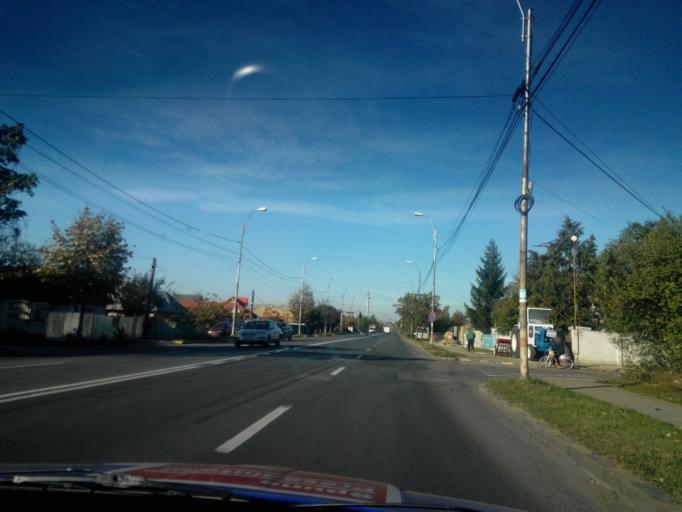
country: RO
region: Bacau
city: Margineni-Munteni
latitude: 46.5857
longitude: 26.9302
